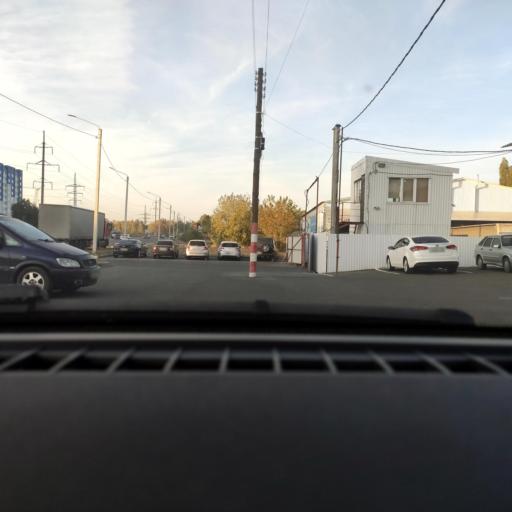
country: RU
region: Voronezj
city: Maslovka
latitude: 51.5923
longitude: 39.2489
